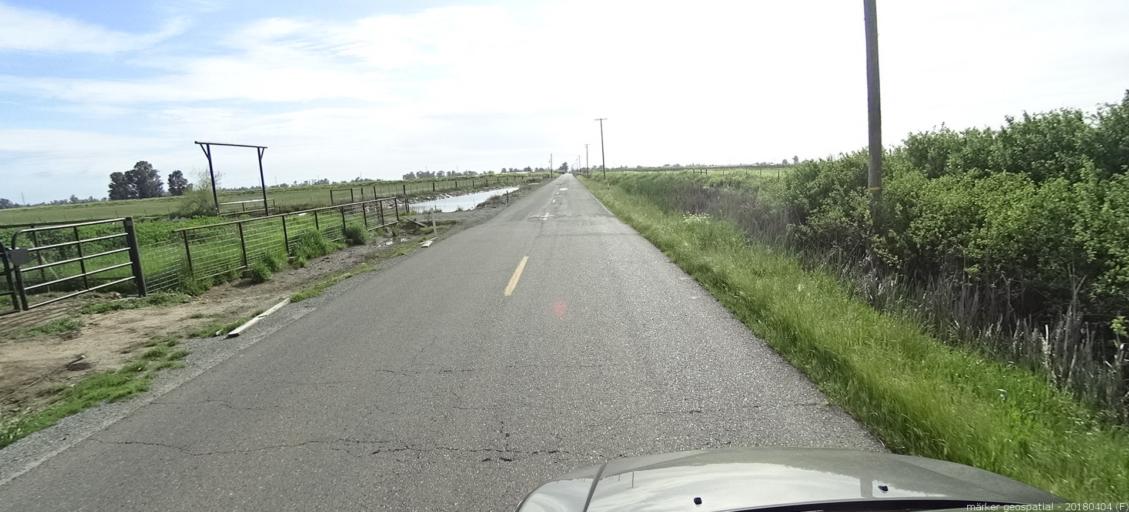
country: US
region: California
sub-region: Sacramento County
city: Herald
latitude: 38.3256
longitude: -121.2587
